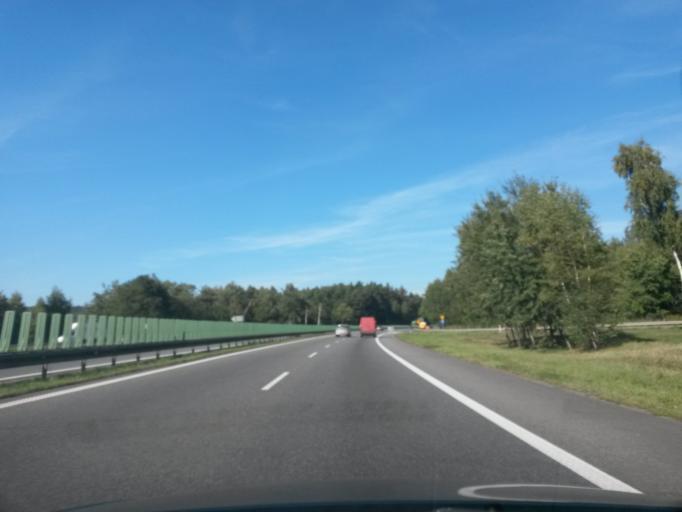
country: PL
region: Lesser Poland Voivodeship
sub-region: Krakow
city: Sidzina
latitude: 49.9980
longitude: 19.8547
